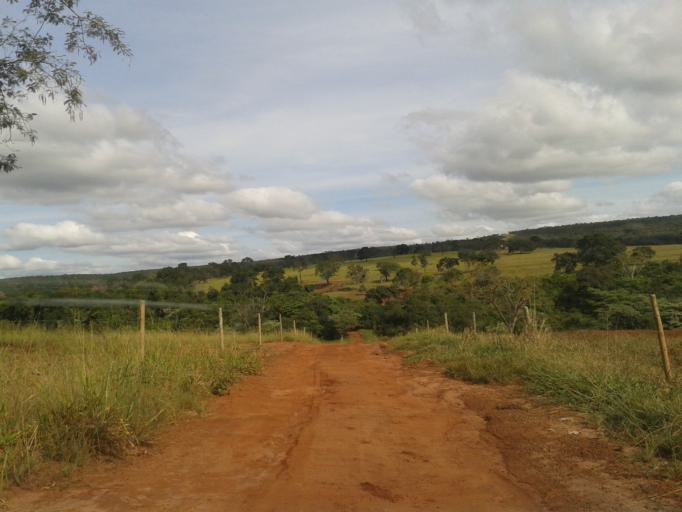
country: BR
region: Minas Gerais
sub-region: Campina Verde
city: Campina Verde
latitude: -19.4273
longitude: -49.7107
